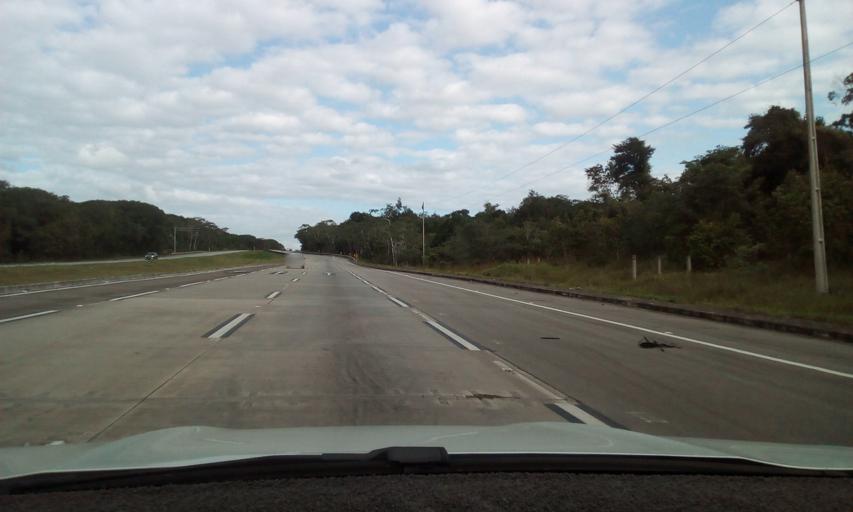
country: BR
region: Paraiba
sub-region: Mamanguape
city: Mamanguape
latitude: -6.9630
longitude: -35.0862
